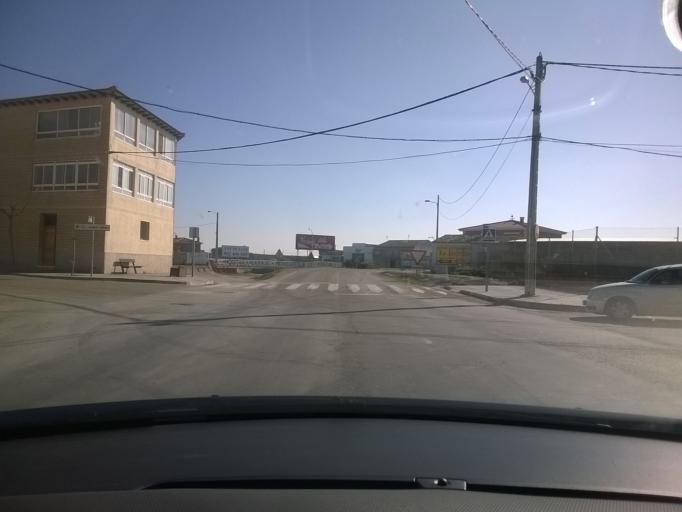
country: ES
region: Aragon
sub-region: Provincia de Zaragoza
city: Bujaraloz
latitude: 41.4976
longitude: -0.1561
